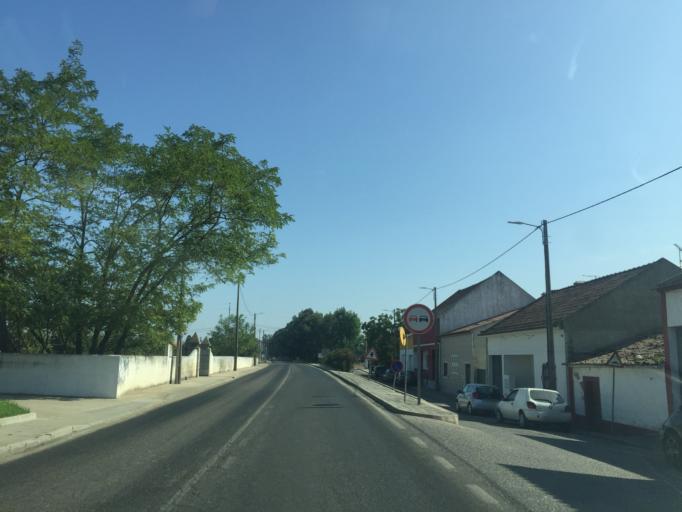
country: PT
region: Santarem
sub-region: Santarem
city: Santarem
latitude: 39.1459
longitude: -8.6825
